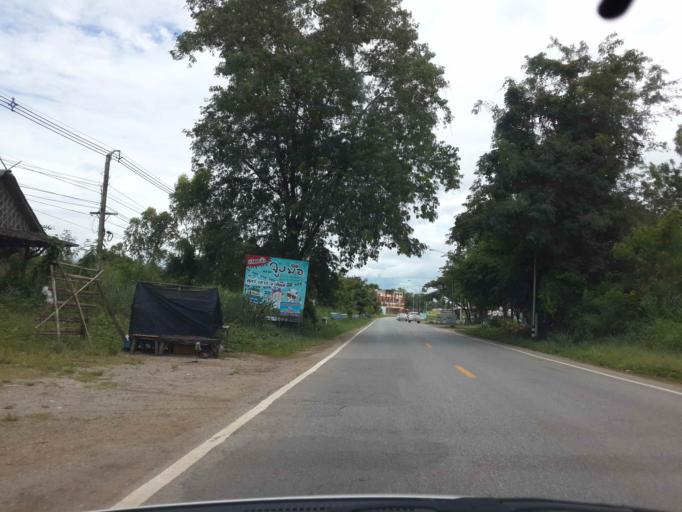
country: TH
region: Ratchaburi
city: Suan Phueng
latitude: 13.5452
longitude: 99.3207
